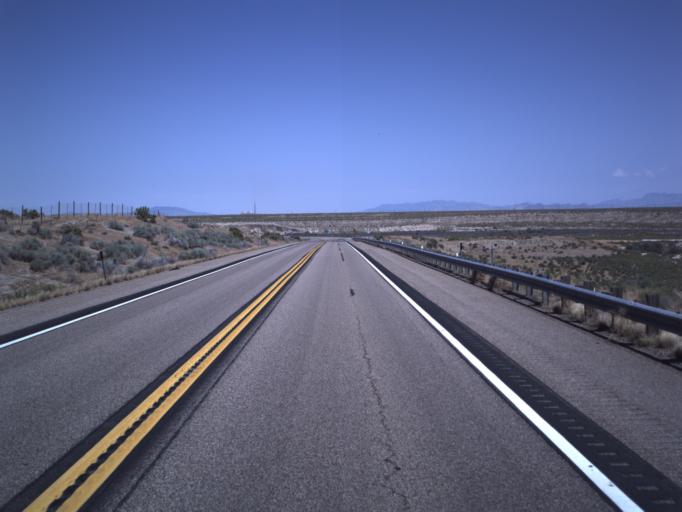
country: US
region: Utah
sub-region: Millard County
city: Delta
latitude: 39.3921
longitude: -112.5007
